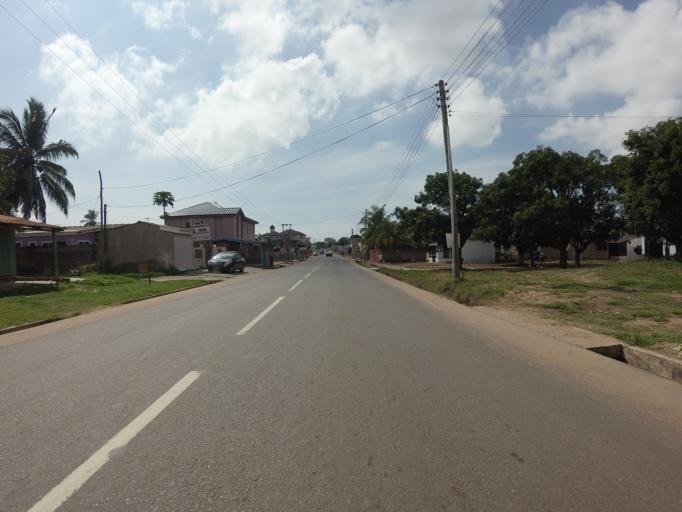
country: GH
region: Greater Accra
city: Nungua
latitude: 5.6107
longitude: -0.0878
